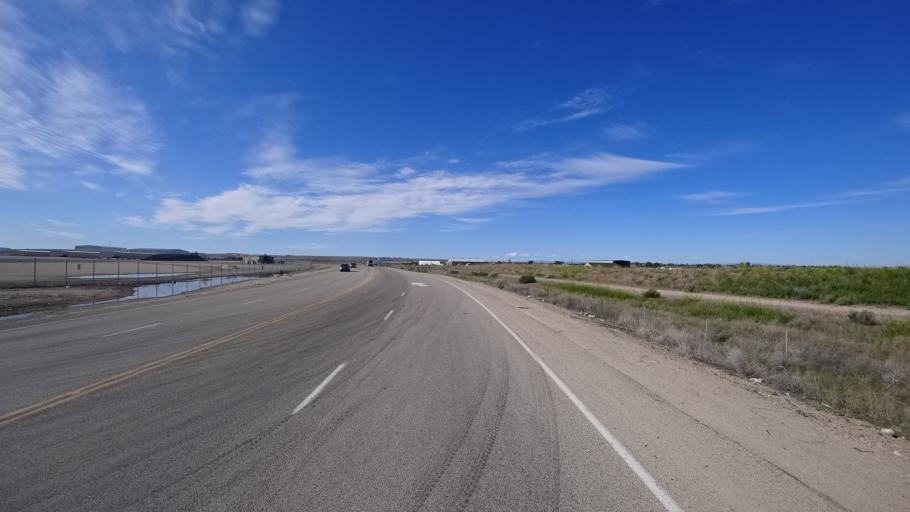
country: US
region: Idaho
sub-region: Ada County
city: Garden City
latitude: 43.5718
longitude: -116.2492
